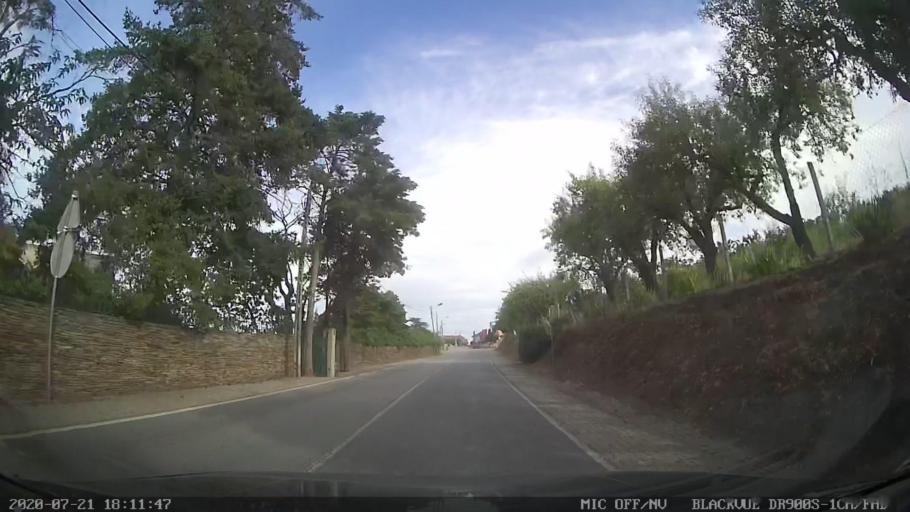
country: PT
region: Viseu
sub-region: Sao Joao da Pesqueira
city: Sao Joao da Pesqueira
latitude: 41.1412
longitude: -7.3971
